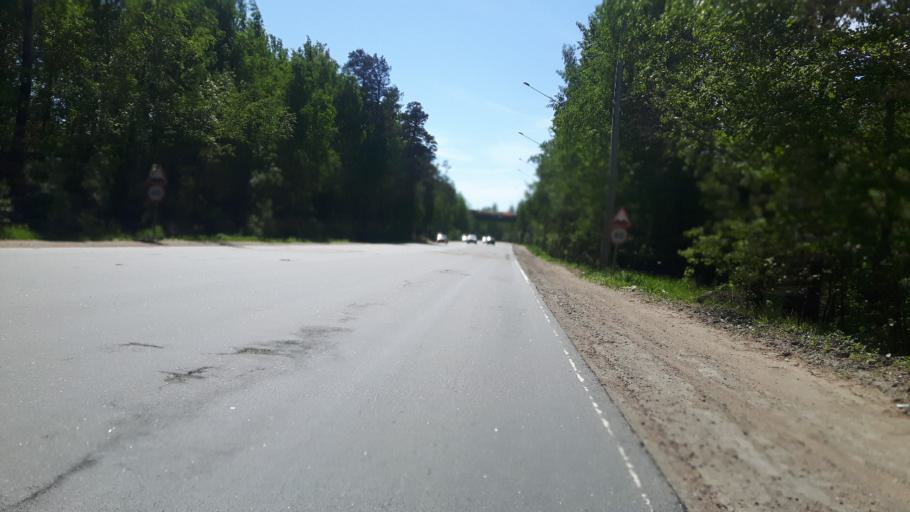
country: RU
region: Leningrad
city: Sosnovyy Bor
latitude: 59.8660
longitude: 29.0718
